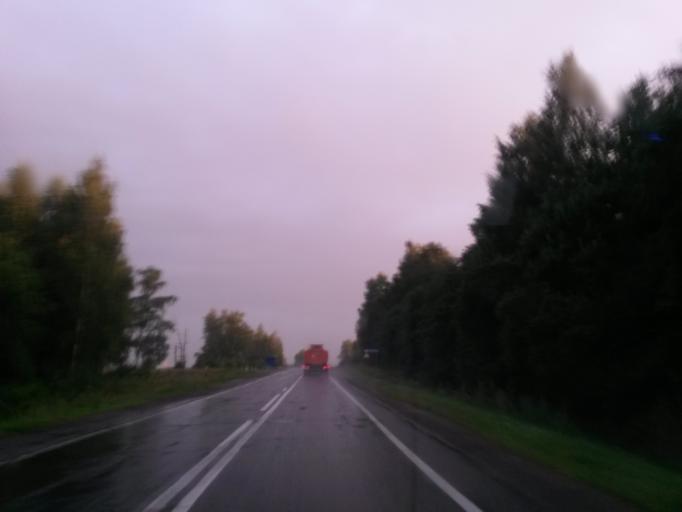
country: RU
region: Jaroslavl
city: Gavrilov-Yam
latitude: 57.3806
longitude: 39.9101
